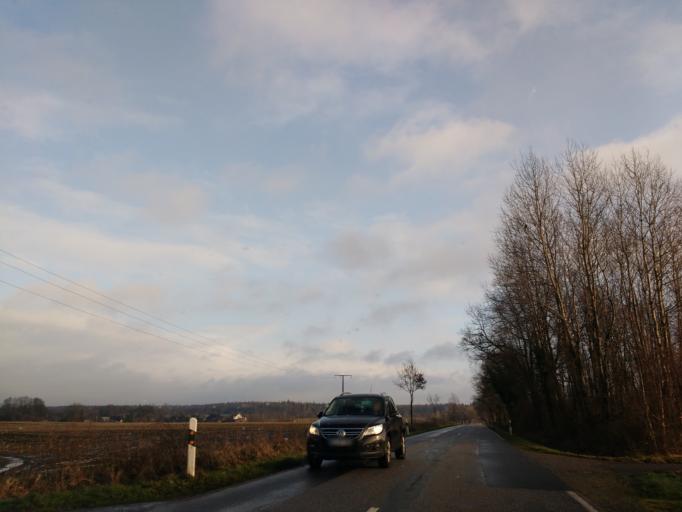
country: DE
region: Schleswig-Holstein
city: Oldenhutten
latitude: 54.1705
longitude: 9.7251
